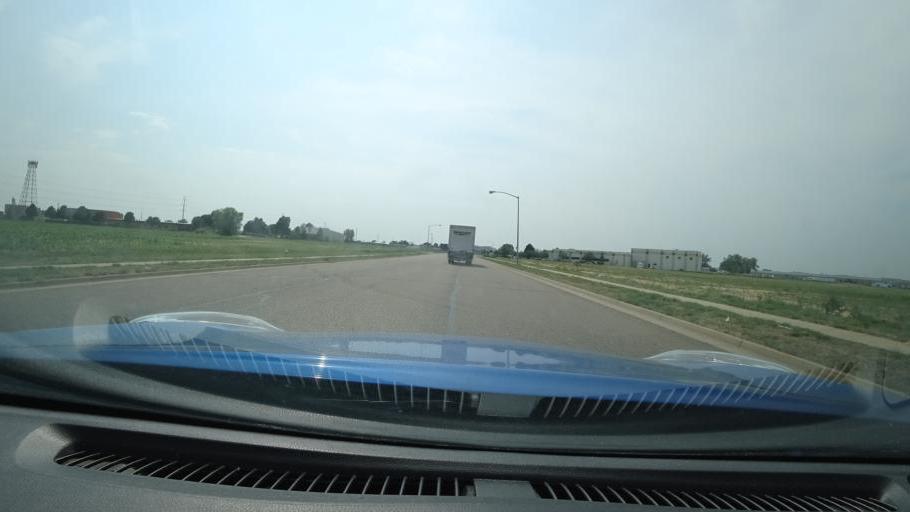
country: US
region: Colorado
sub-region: Adams County
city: Aurora
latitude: 39.7568
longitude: -104.7375
